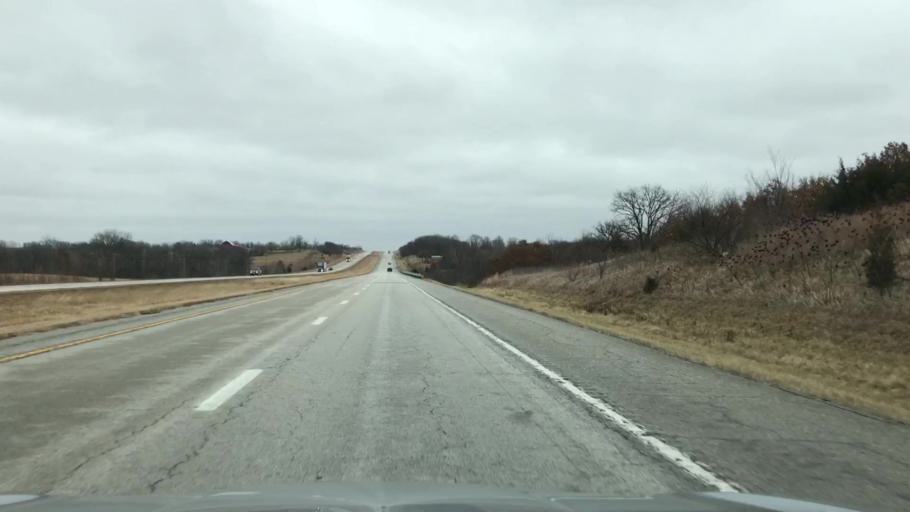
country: US
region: Missouri
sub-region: Clinton County
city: Cameron
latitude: 39.7504
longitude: -94.1225
